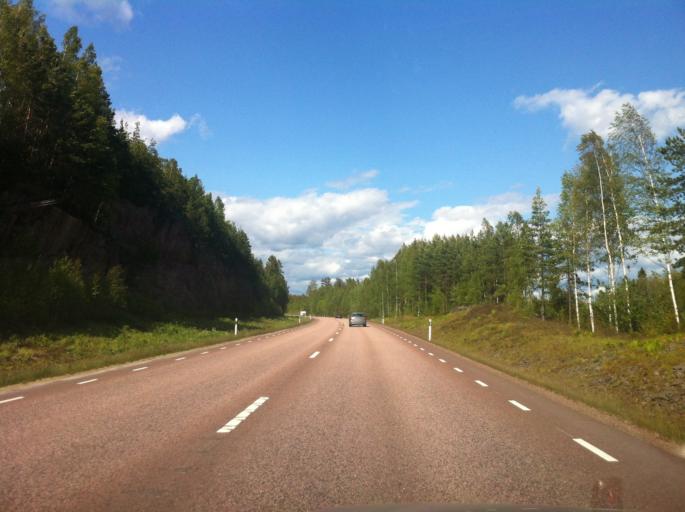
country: SE
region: Vaermland
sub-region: Storfors Kommun
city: Storfors
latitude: 59.4052
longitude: 14.2188
